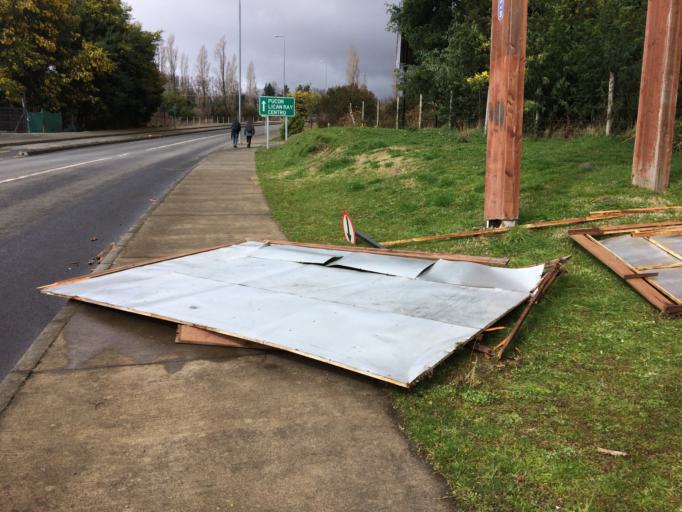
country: CL
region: Araucania
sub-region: Provincia de Cautin
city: Villarrica
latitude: -39.2928
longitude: -72.2137
